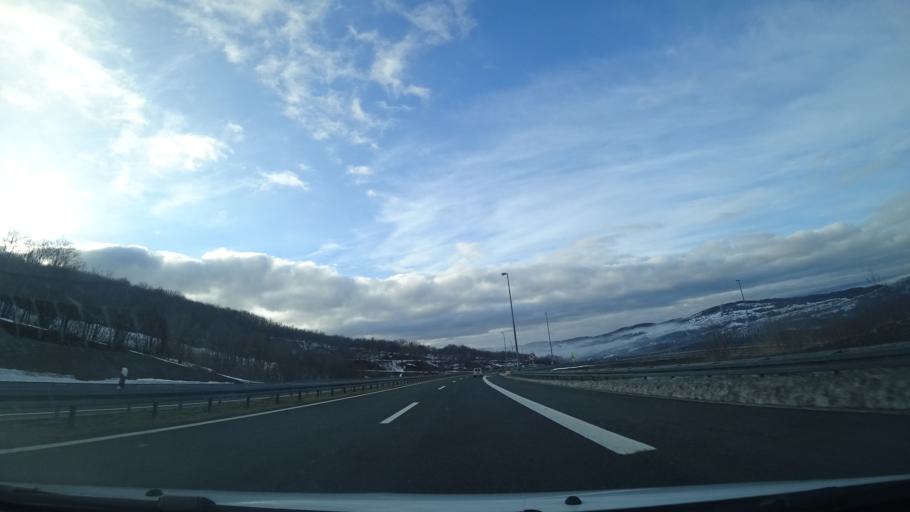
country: HR
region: Licko-Senjska
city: Brinje
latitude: 45.0674
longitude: 15.2075
